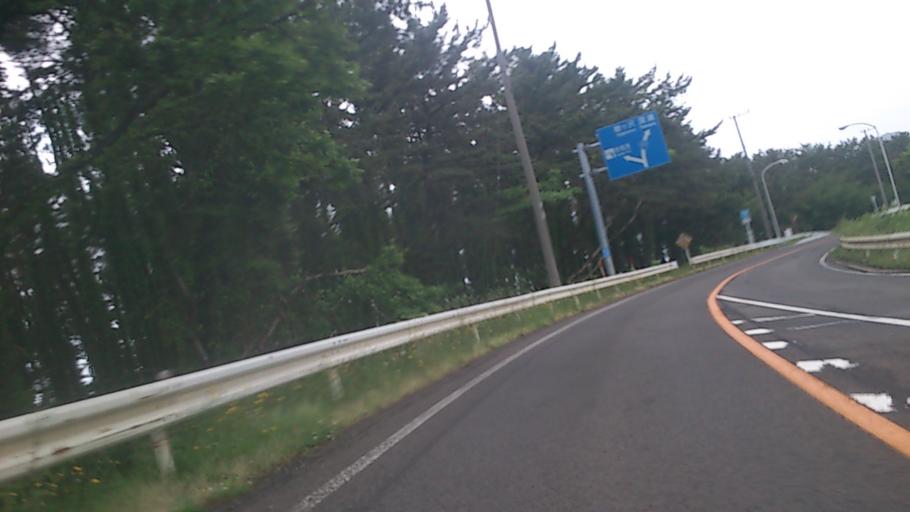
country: JP
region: Akita
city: Noshiromachi
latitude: 40.3901
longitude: 139.9822
